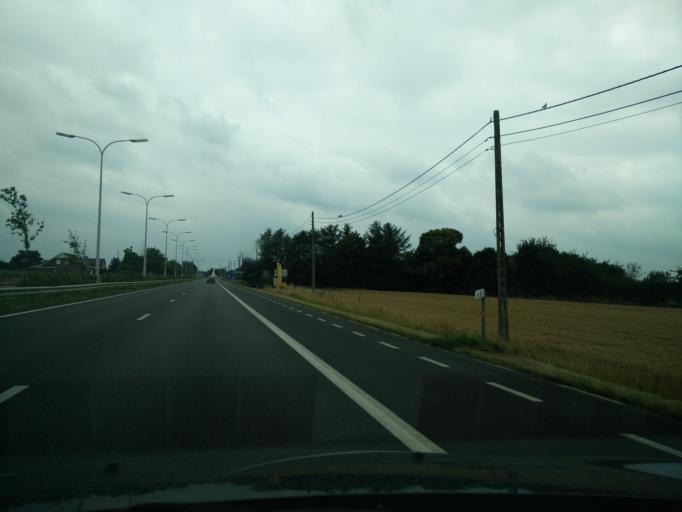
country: BE
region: Flanders
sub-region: Provincie Oost-Vlaanderen
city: Oudenaarde
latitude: 50.8850
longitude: 3.6159
